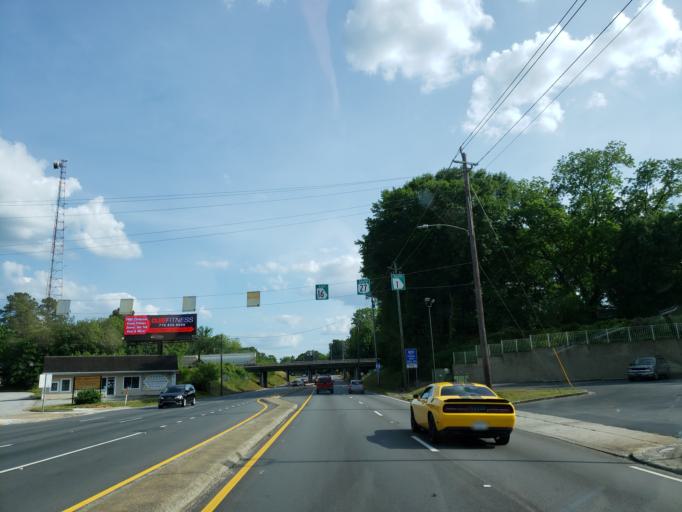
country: US
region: Georgia
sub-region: Carroll County
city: Carrollton
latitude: 33.5778
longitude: -85.0789
